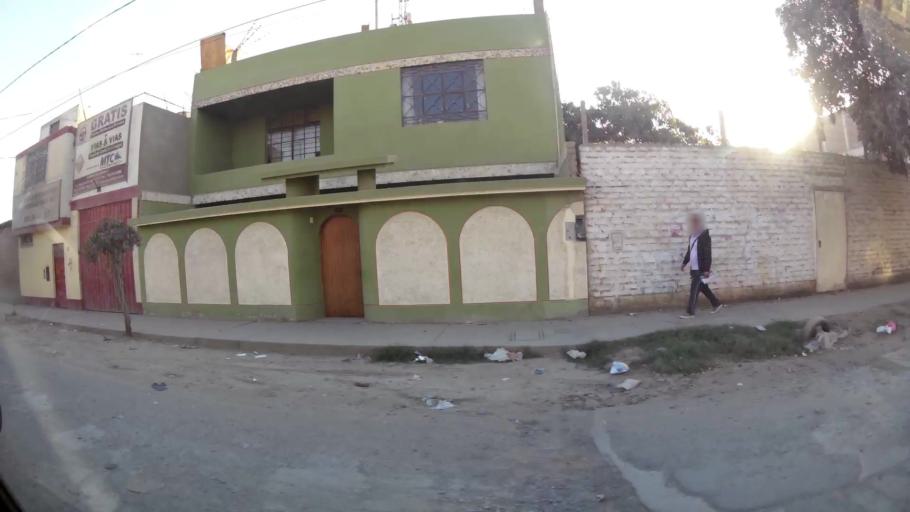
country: PE
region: Ica
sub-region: Provincia de Ica
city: Ica
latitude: -14.0640
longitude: -75.7360
